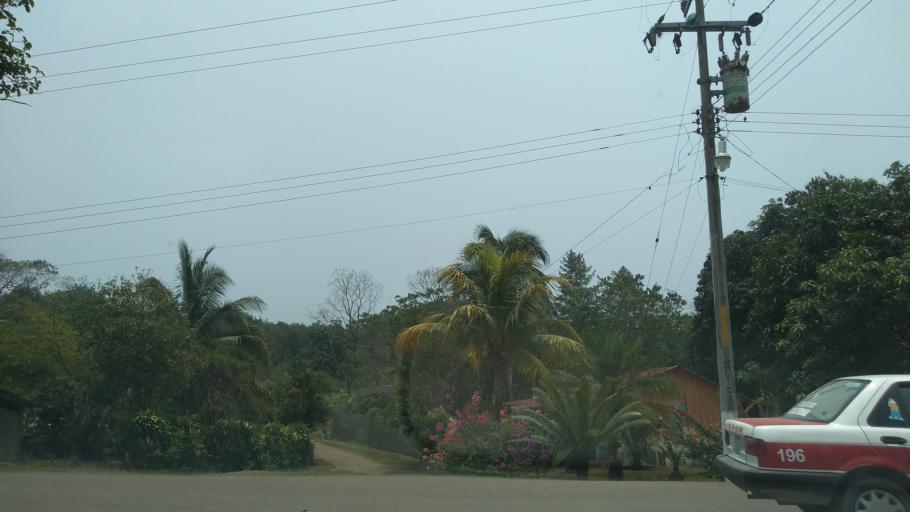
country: MX
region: Veracruz
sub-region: Tezonapa
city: Laguna Chica (Pueblo Nuevo)
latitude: 18.5132
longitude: -96.7620
